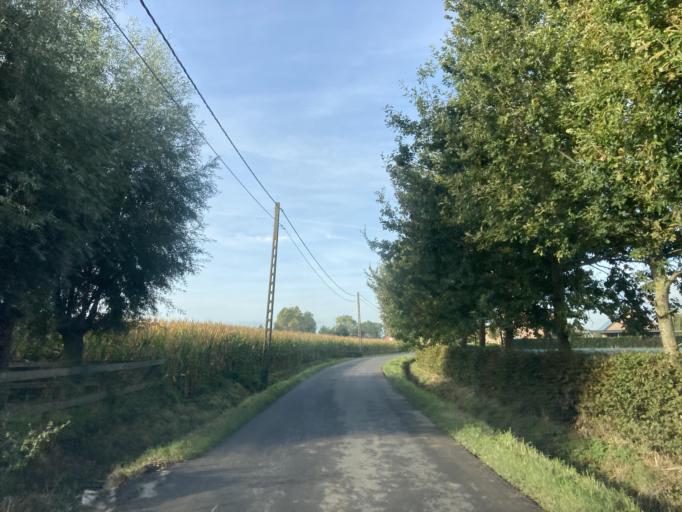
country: BE
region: Flanders
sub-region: Provincie West-Vlaanderen
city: Tielt
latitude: 50.9978
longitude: 3.3009
